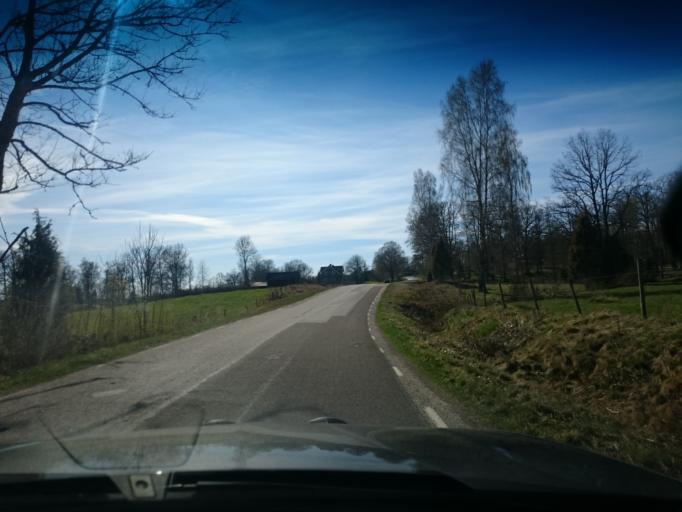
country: SE
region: Kalmar
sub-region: Hultsfreds Kommun
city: Virserum
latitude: 57.3302
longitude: 15.5004
